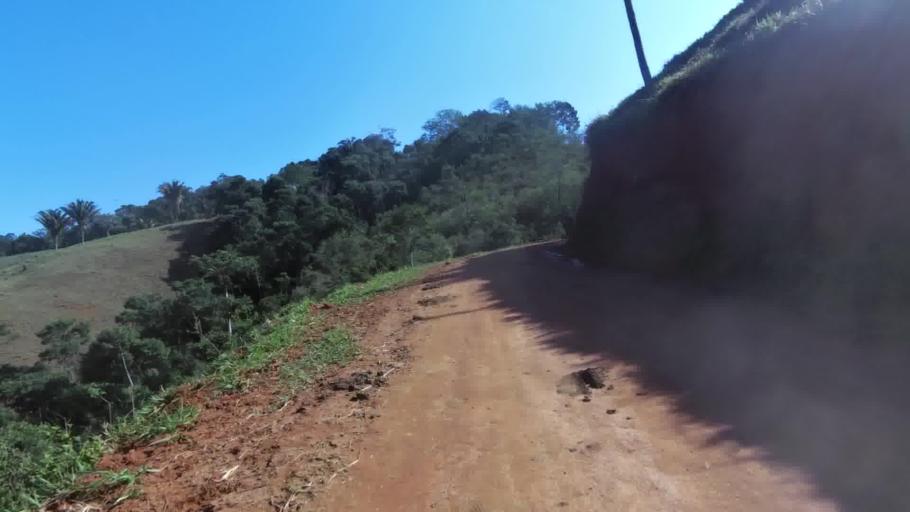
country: BR
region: Espirito Santo
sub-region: Alfredo Chaves
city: Alfredo Chaves
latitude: -20.6725
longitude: -40.7818
